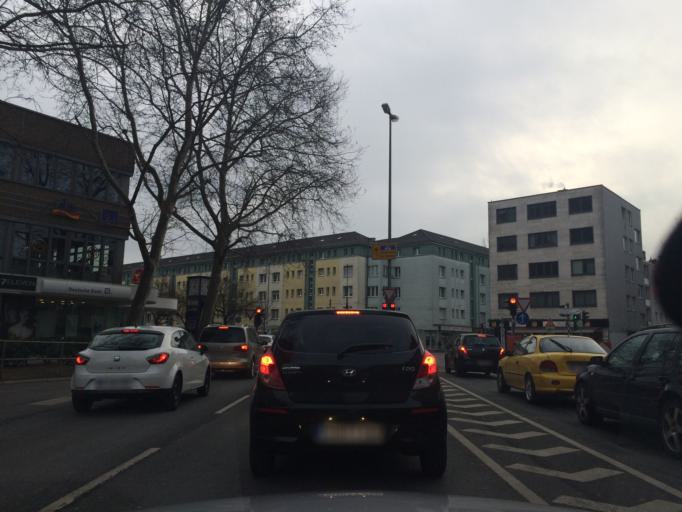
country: DE
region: Hesse
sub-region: Regierungsbezirk Darmstadt
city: Frankfurt am Main
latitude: 50.1033
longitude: 8.6910
